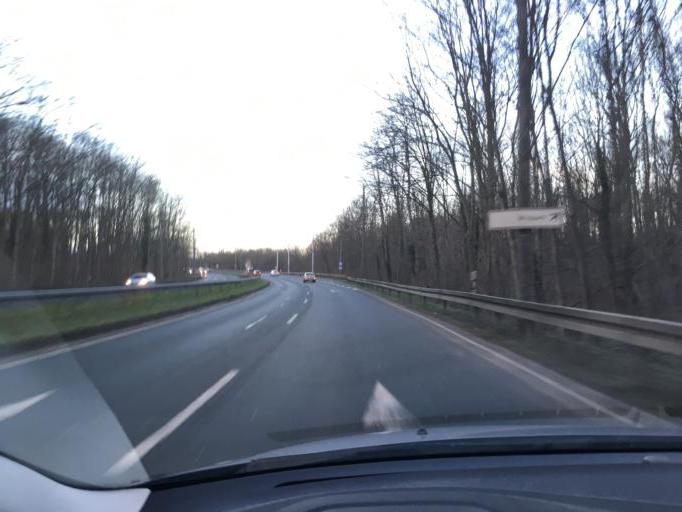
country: DE
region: Saxony
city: Markkleeberg
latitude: 51.2982
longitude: 12.3768
